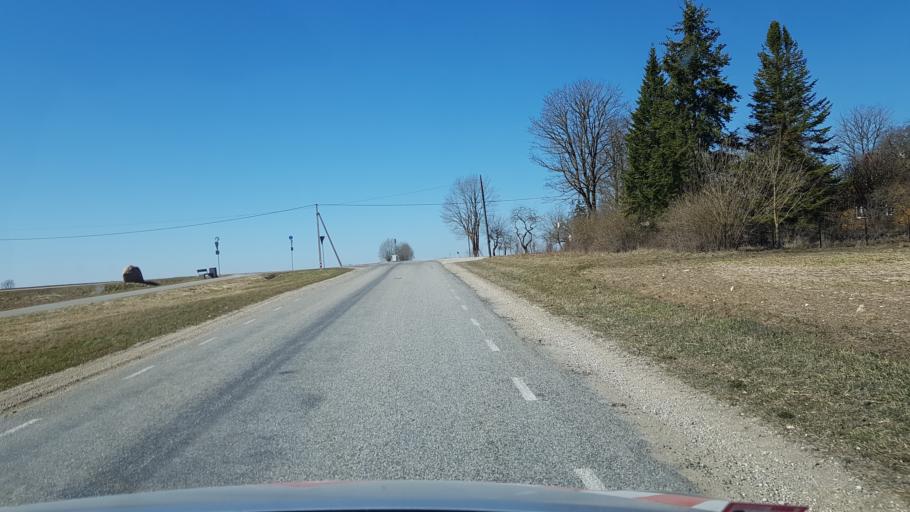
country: EE
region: Laeaene-Virumaa
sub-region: Vinni vald
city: Vinni
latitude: 59.0692
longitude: 26.5292
